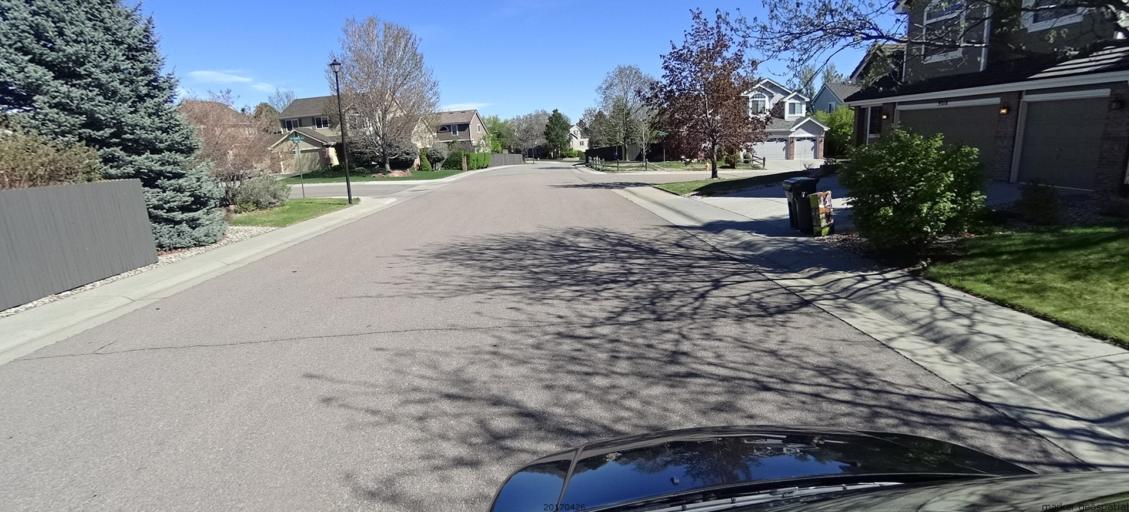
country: US
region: Colorado
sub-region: Douglas County
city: Carriage Club
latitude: 39.5430
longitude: -104.9030
